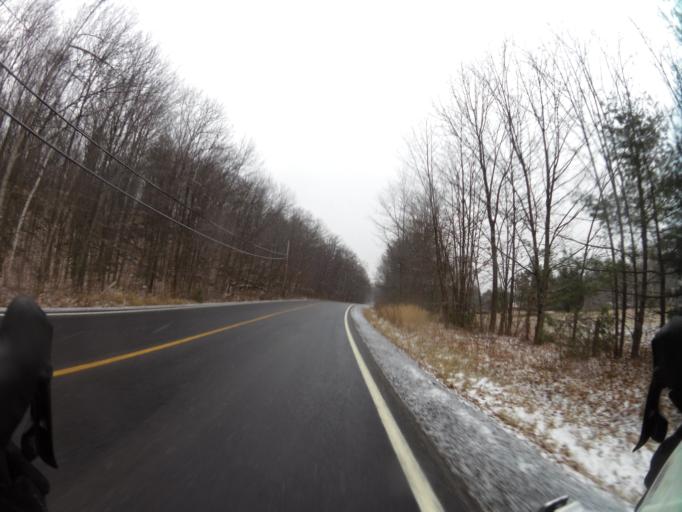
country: CA
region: Quebec
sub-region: Outaouais
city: Gatineau
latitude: 45.4985
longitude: -75.8215
